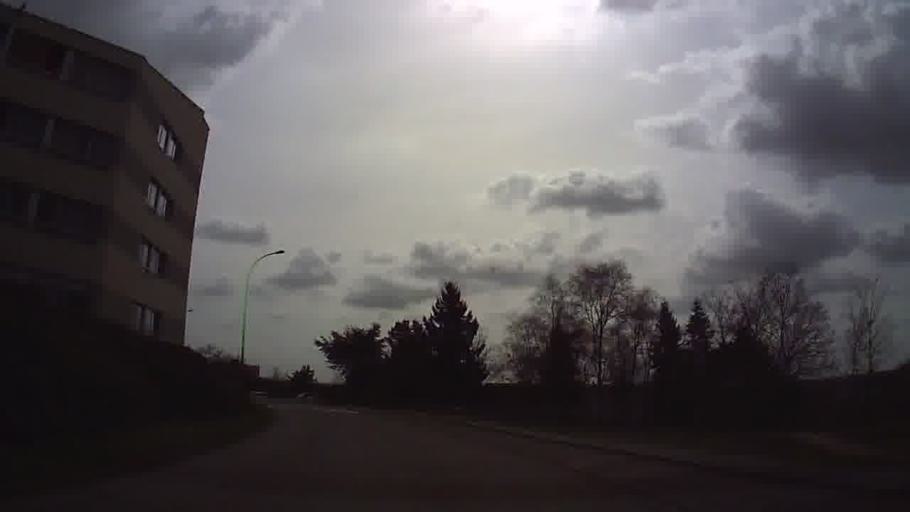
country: FR
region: Brittany
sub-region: Departement d'Ille-et-Vilaine
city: Rennes
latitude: 48.1231
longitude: -1.6453
